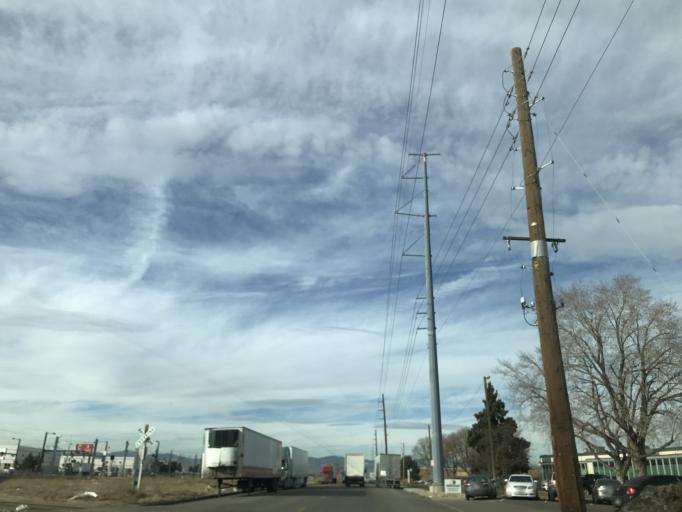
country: US
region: Colorado
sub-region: Adams County
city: Commerce City
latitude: 39.7737
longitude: -104.9105
